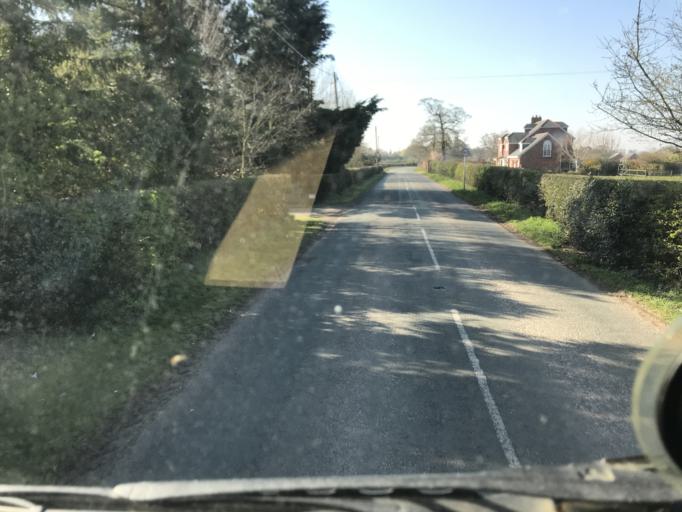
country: GB
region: England
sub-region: Cheshire West and Chester
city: Waverton
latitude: 53.1644
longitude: -2.8252
